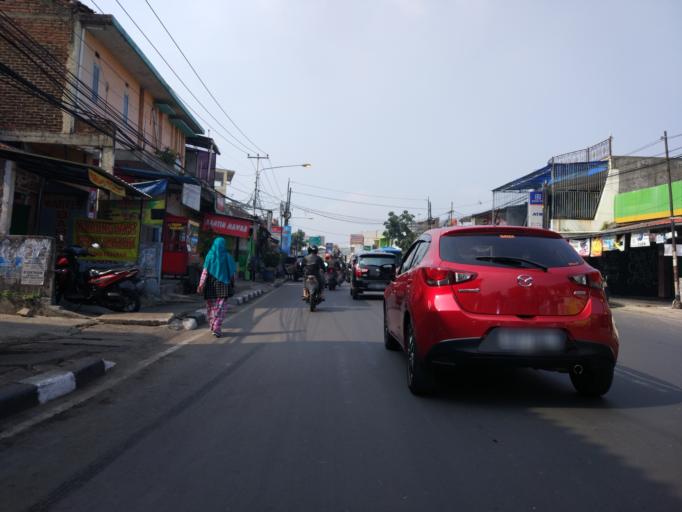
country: ID
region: West Java
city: Cileunyi
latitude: -6.9329
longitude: 107.7161
